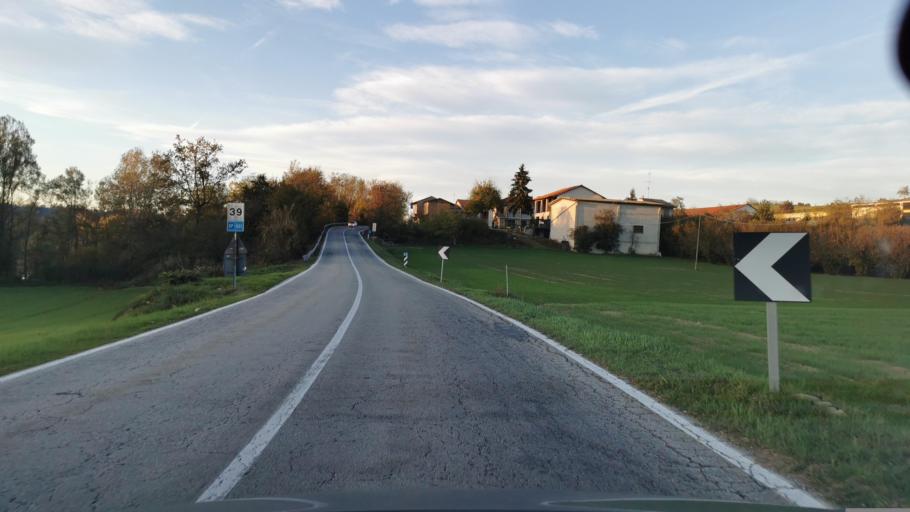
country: IT
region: Piedmont
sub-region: Provincia di Cuneo
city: Narzole
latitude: 44.5939
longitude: 7.8942
